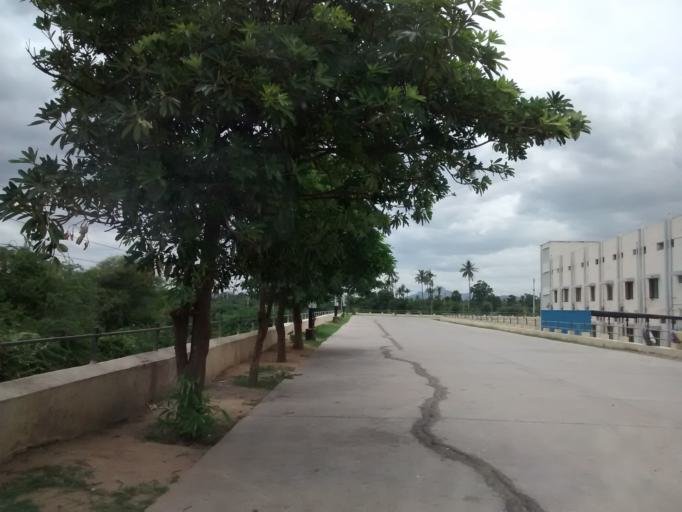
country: IN
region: Andhra Pradesh
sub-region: Chittoor
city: Chittoor
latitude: 13.2751
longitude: 79.0335
